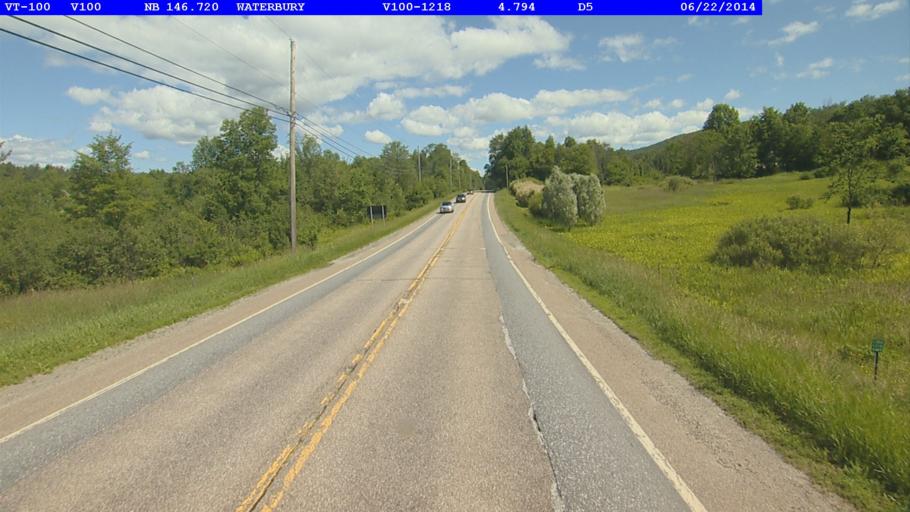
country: US
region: Vermont
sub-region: Washington County
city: Waterbury
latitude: 44.3981
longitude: -72.7192
